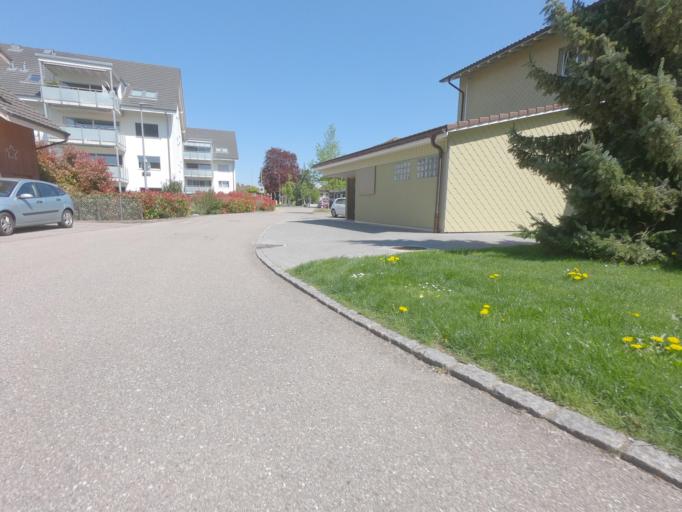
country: CH
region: Bern
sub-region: Biel/Bienne District
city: Brugg
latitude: 47.1211
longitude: 7.2874
